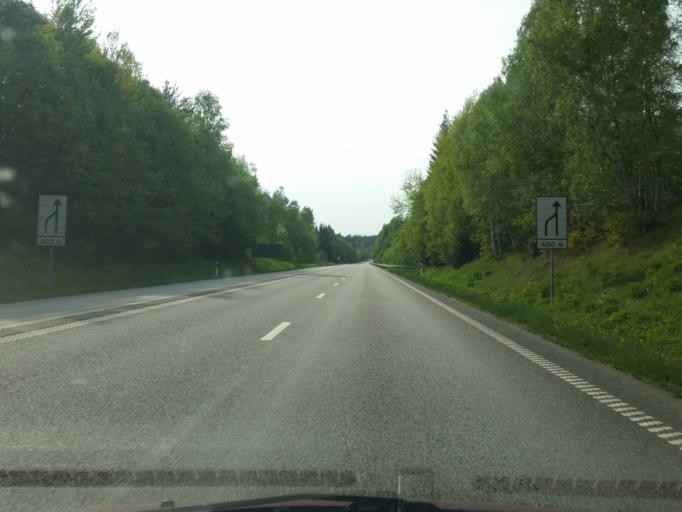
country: SE
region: Vaestra Goetaland
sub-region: Ulricehamns Kommun
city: Ulricehamn
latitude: 57.8028
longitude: 13.3381
